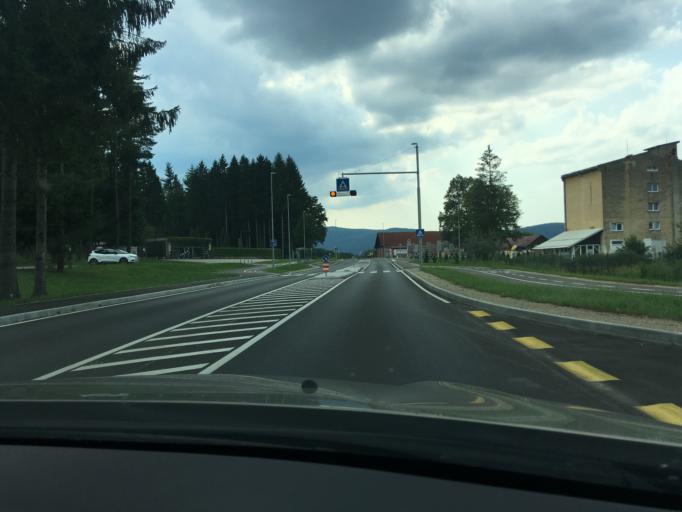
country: SI
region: Novo Mesto
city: Novo Mesto
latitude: 45.7926
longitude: 15.1382
